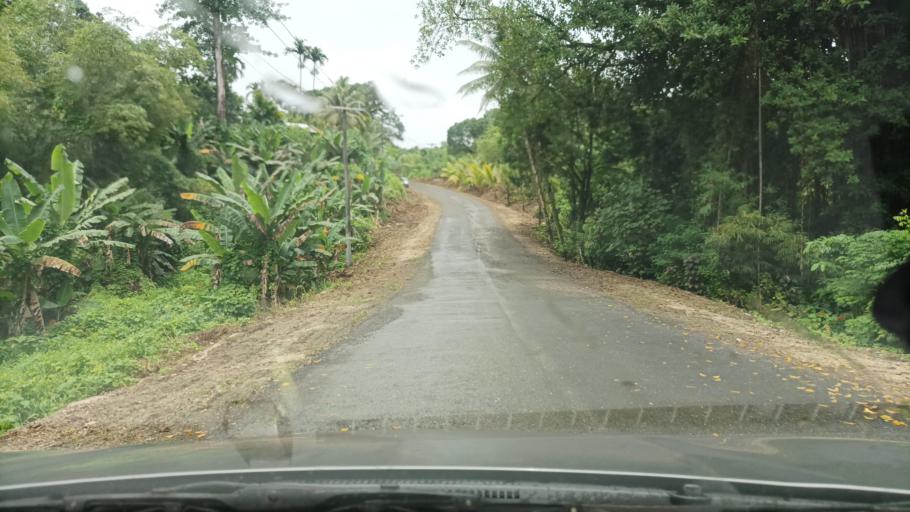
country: FM
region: Pohnpei
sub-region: Madolenihm Municipality
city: Madolenihm Municipality Government
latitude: 6.8148
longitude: 158.2353
